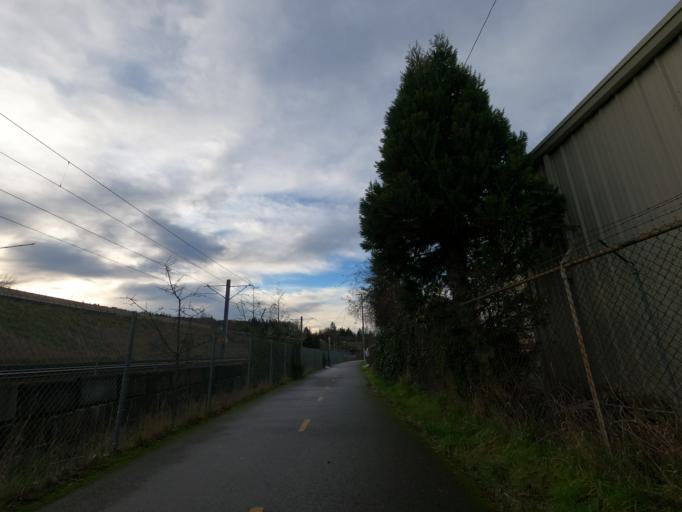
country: US
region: Oregon
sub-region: Multnomah County
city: Lents
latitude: 45.4696
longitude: -122.5662
